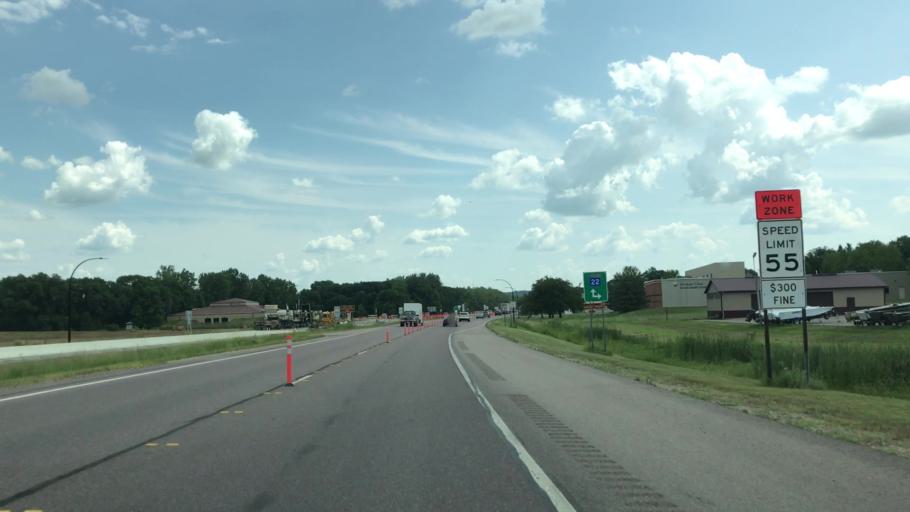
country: US
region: Minnesota
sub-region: Nicollet County
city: Saint Peter
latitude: 44.3514
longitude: -93.9528
